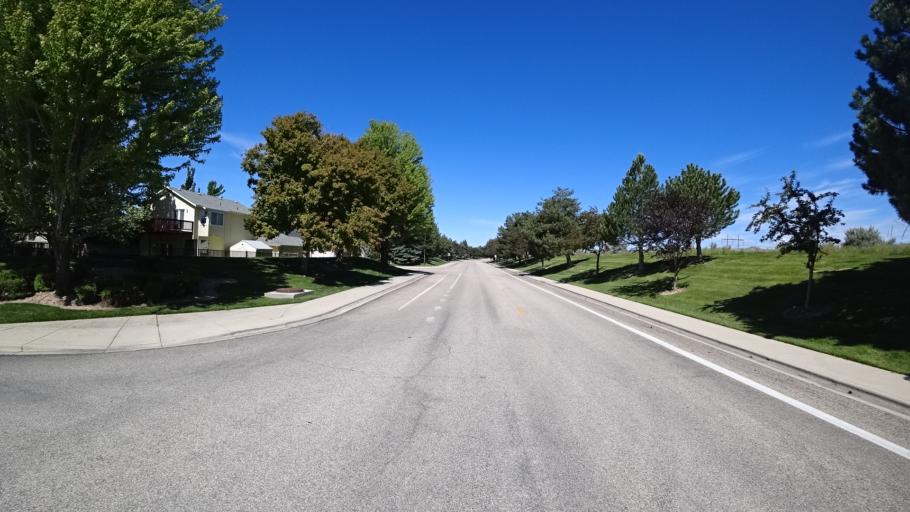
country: US
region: Idaho
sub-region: Ada County
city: Boise
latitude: 43.5482
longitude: -116.1189
